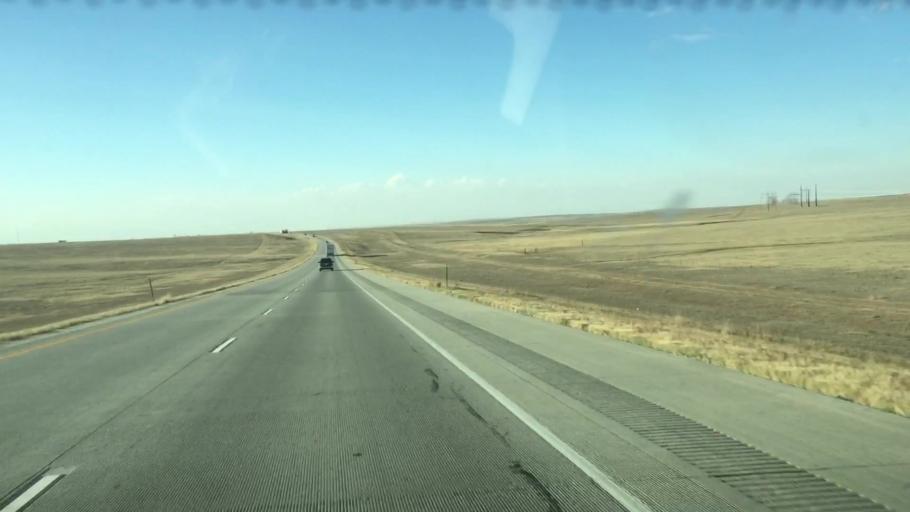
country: US
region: Colorado
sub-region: Lincoln County
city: Limon
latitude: 39.4073
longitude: -103.8979
